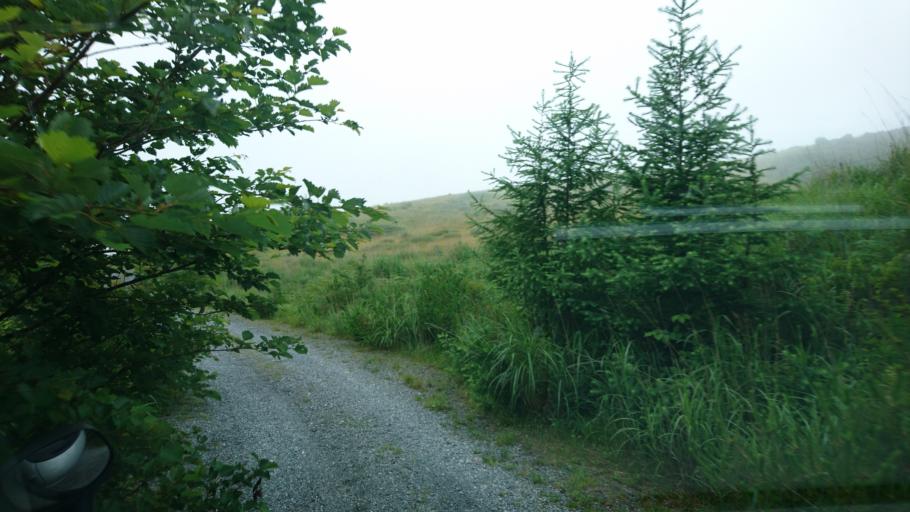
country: JP
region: Iwate
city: Ofunato
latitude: 39.1711
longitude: 141.7881
